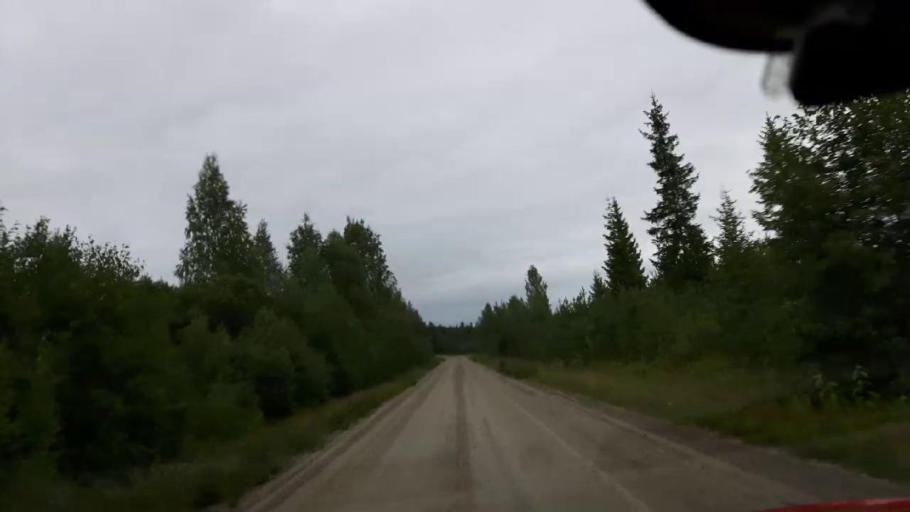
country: SE
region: Vaesternorrland
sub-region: Ange Kommun
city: Ange
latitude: 62.8055
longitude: 15.7467
